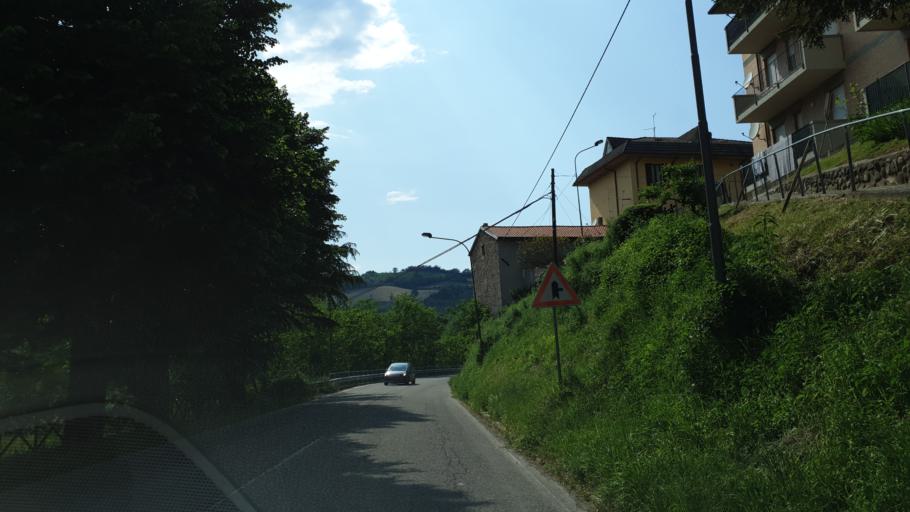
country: IT
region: Emilia-Romagna
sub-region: Forli-Cesena
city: Sarsina
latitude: 43.9245
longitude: 12.1564
